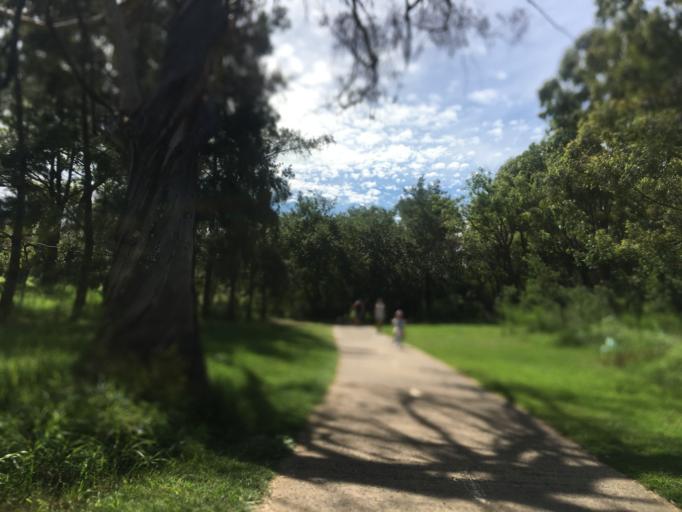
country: AU
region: New South Wales
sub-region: Camden
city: Elderslie
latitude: -34.0640
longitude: 150.6996
